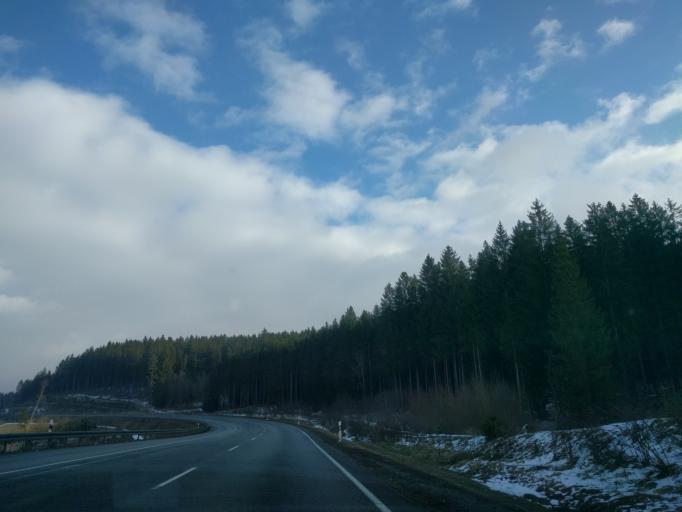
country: DE
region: Bavaria
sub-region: Lower Bavaria
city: Regen
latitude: 48.9814
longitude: 13.1613
